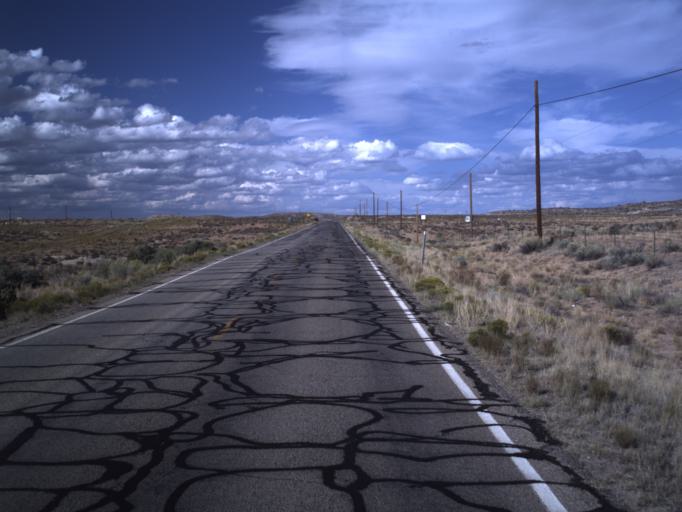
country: US
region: Utah
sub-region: San Juan County
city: Blanding
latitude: 37.2819
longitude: -109.2935
